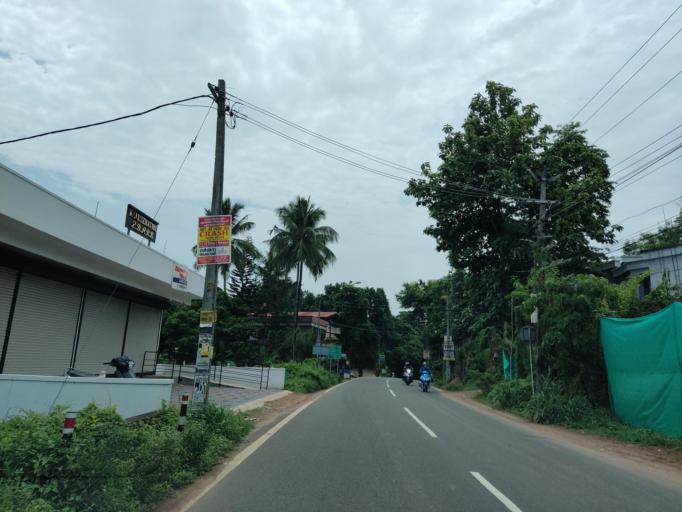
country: IN
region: Kerala
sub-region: Alappuzha
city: Chengannur
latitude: 9.3007
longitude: 76.6273
